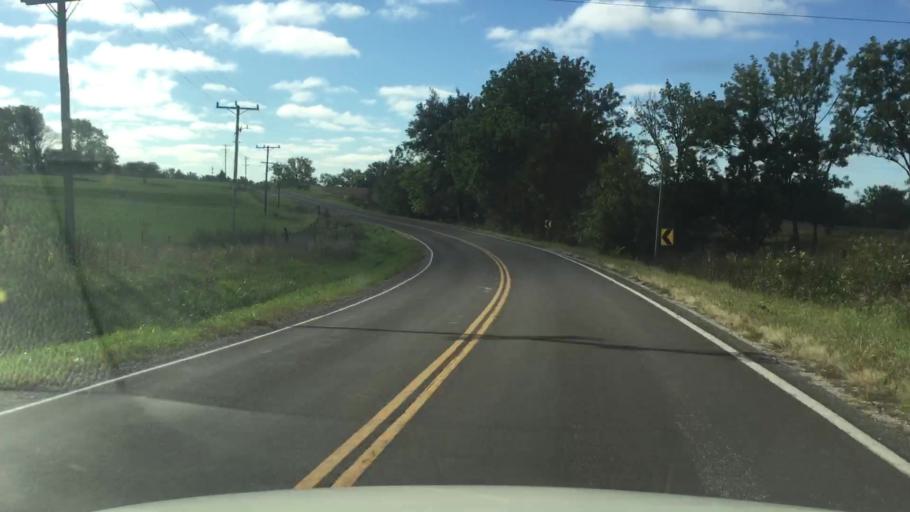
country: US
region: Missouri
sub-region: Howard County
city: New Franklin
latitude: 39.0644
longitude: -92.7461
